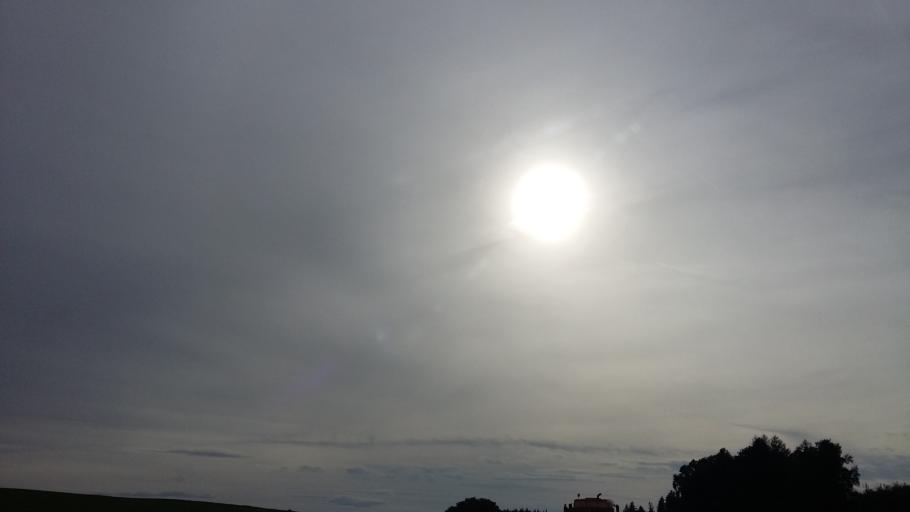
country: DE
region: Bavaria
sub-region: Upper Bavaria
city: Munsing
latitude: 47.9114
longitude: 11.3748
